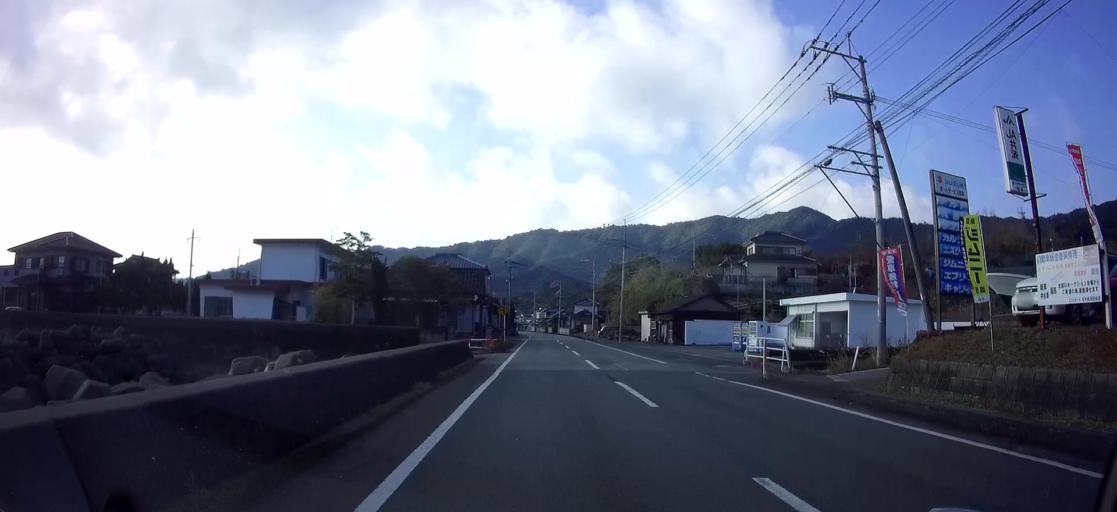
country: JP
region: Kumamoto
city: Minamata
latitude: 32.3899
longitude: 130.3757
